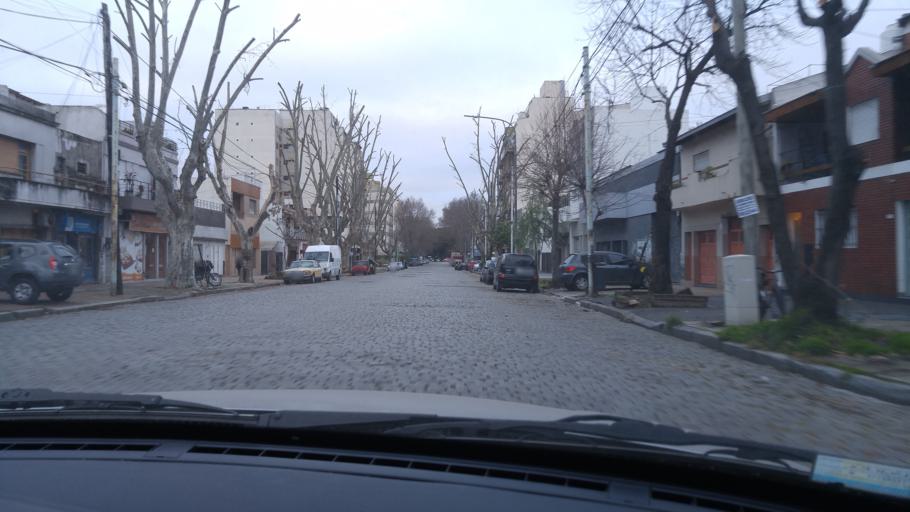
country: AR
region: Buenos Aires F.D.
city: Villa Santa Rita
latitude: -34.6305
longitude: -58.5183
